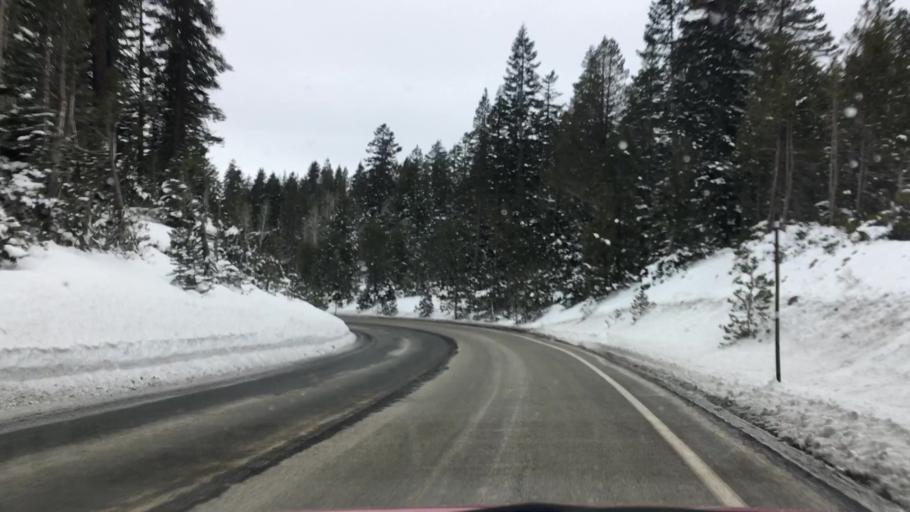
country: US
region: California
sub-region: El Dorado County
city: South Lake Tahoe
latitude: 38.7054
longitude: -120.1107
